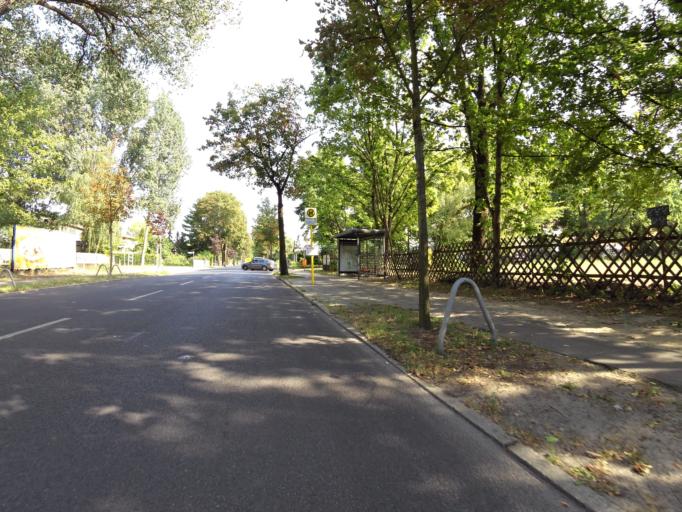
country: DE
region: Berlin
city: Grunau
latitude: 52.4125
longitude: 13.5661
